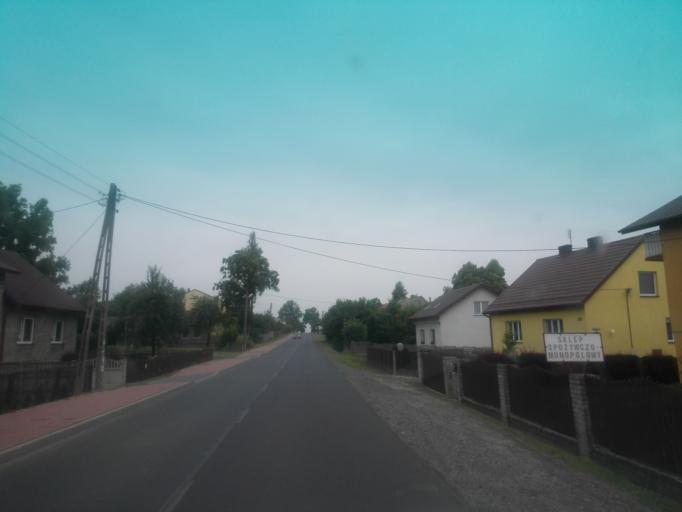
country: PL
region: Silesian Voivodeship
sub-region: Powiat czestochowski
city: Olsztyn
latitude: 50.7707
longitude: 19.2746
